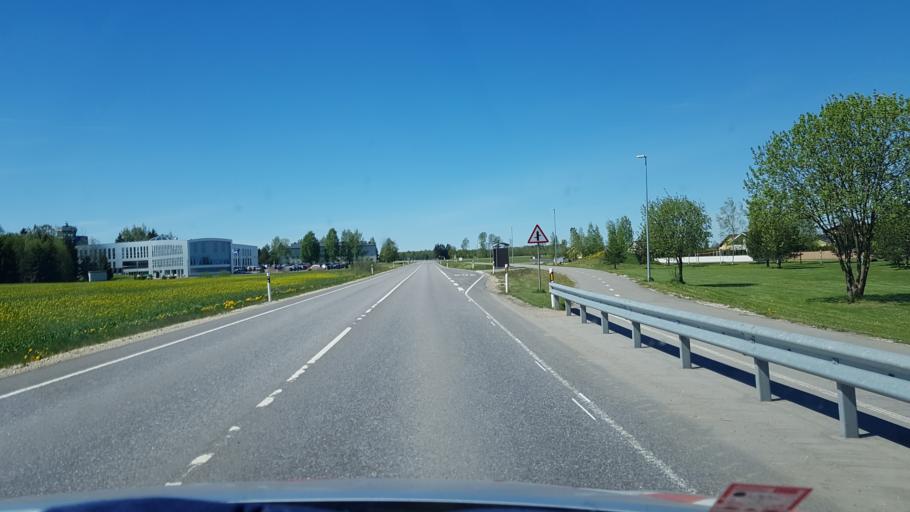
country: EE
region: Tartu
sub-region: UElenurme vald
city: Ulenurme
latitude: 58.3112
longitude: 26.6982
